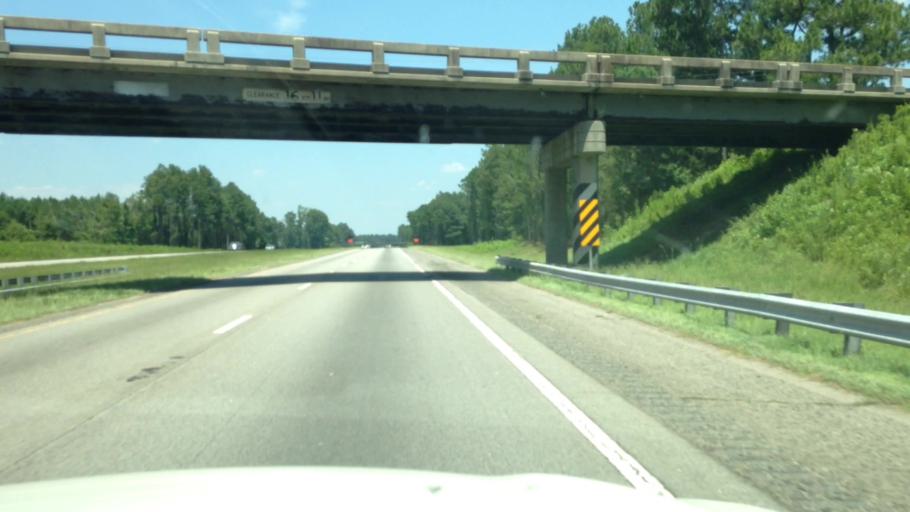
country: US
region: South Carolina
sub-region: Dillon County
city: Dillon
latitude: 34.4799
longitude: -79.3391
